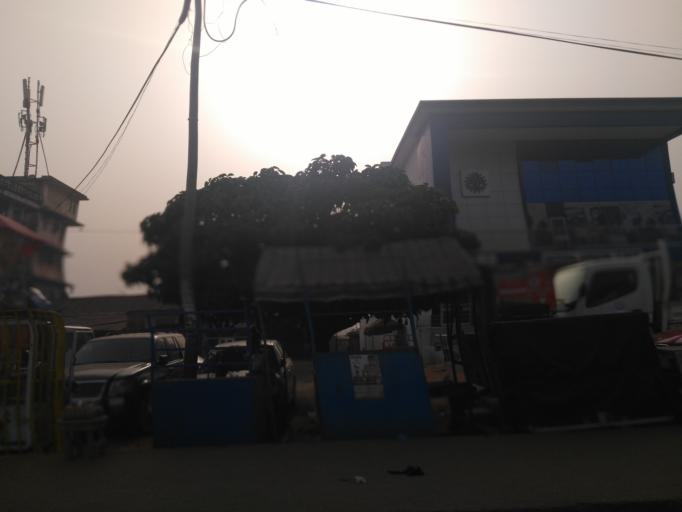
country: GH
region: Ashanti
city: Tafo
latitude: 6.7150
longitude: -1.6294
